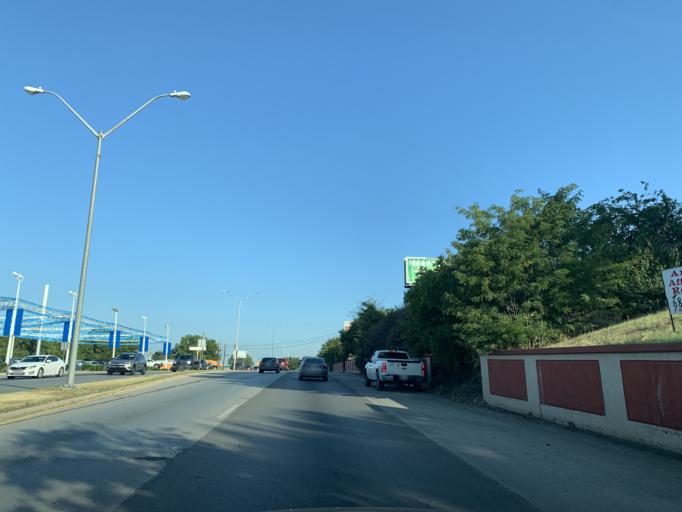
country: US
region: Texas
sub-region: Tarrant County
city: River Oaks
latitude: 32.7691
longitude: -97.3573
